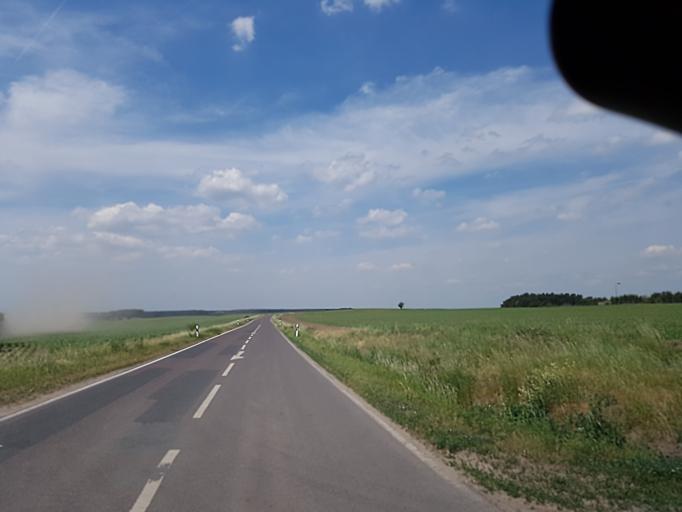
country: DE
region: Brandenburg
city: Gorzke
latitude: 52.1139
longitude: 12.3601
